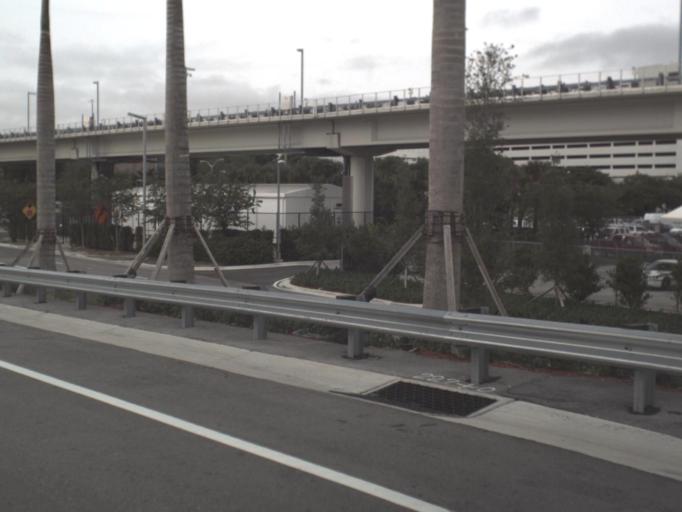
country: US
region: Florida
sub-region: Miami-Dade County
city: Miami Springs
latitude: 25.7950
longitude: -80.2672
